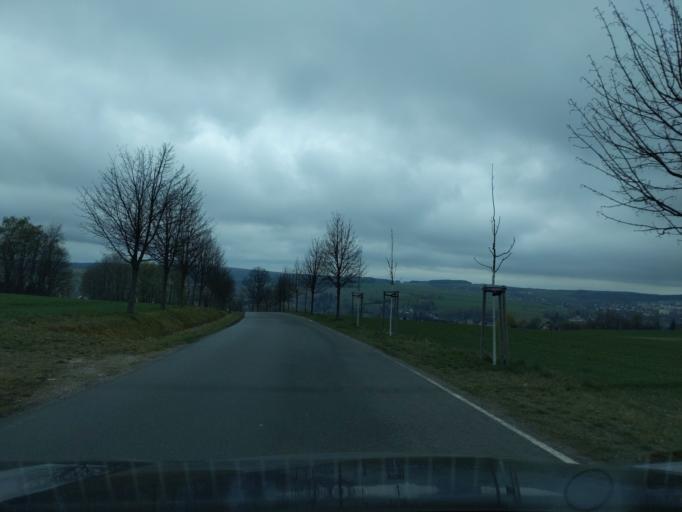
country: DE
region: Saxony
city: Zschorlau
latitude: 50.5799
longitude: 12.6472
